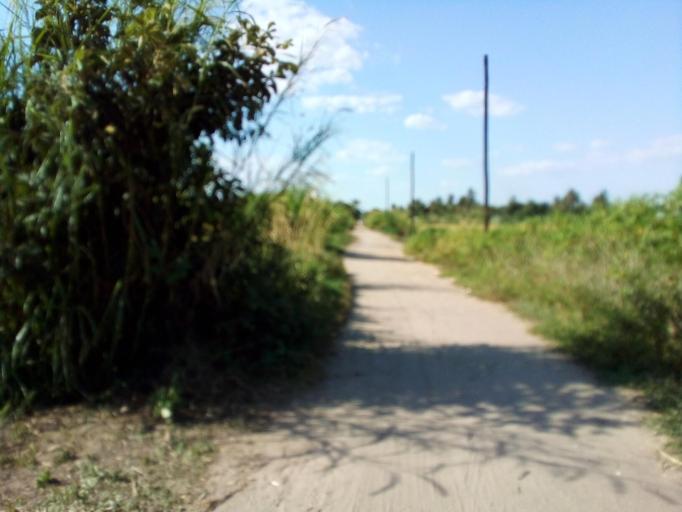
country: MZ
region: Zambezia
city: Quelimane
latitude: -17.5953
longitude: 36.8304
